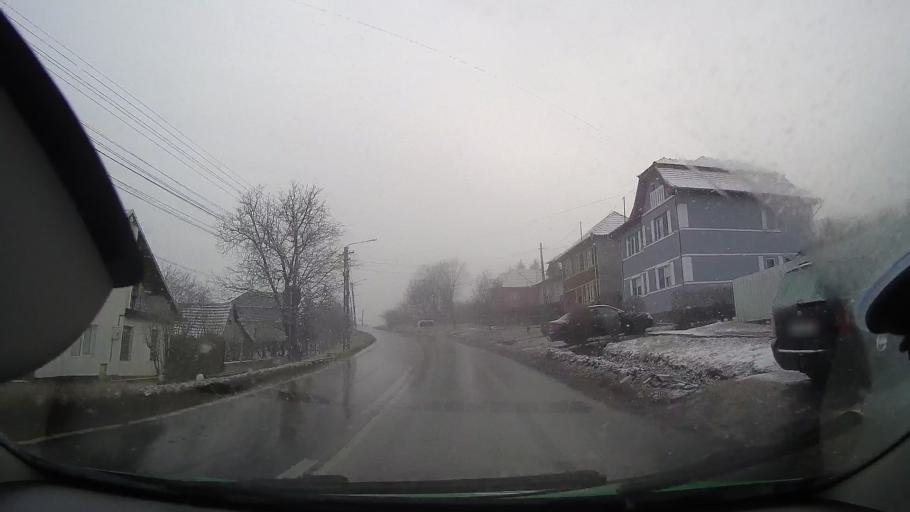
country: RO
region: Mures
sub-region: Comuna Bagaciu
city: Delenii
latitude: 46.2770
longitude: 24.3008
